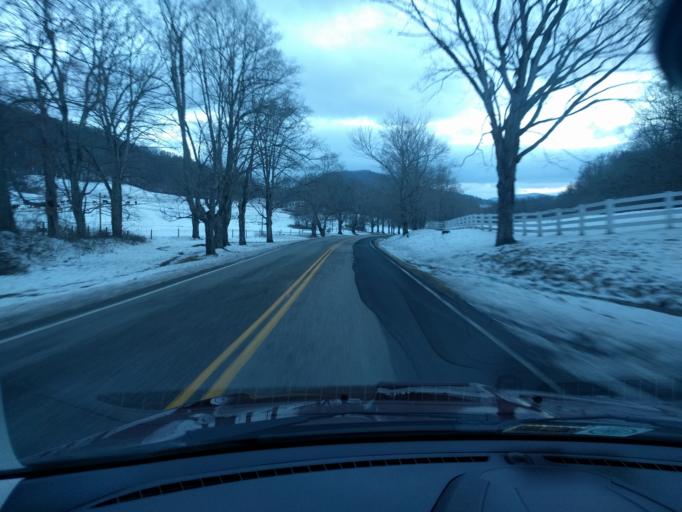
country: US
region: Virginia
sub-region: Bath County
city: Warm Springs
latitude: 37.9852
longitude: -79.8377
